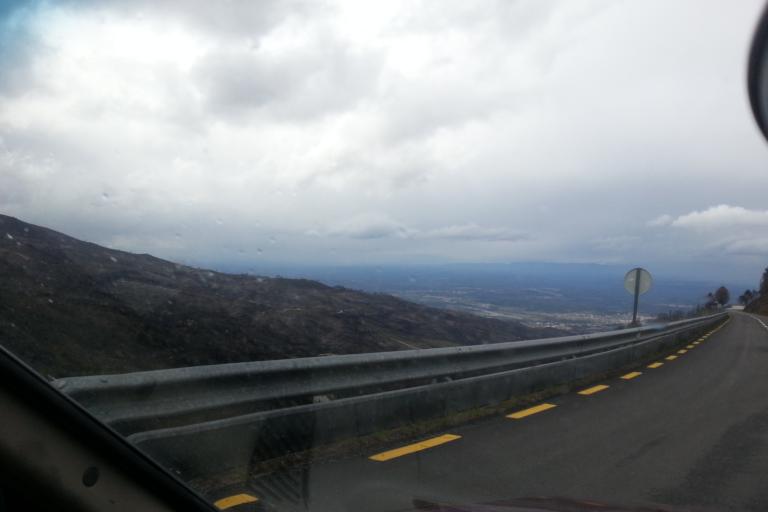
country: PT
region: Guarda
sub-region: Manteigas
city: Manteigas
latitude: 40.4413
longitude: -7.5965
